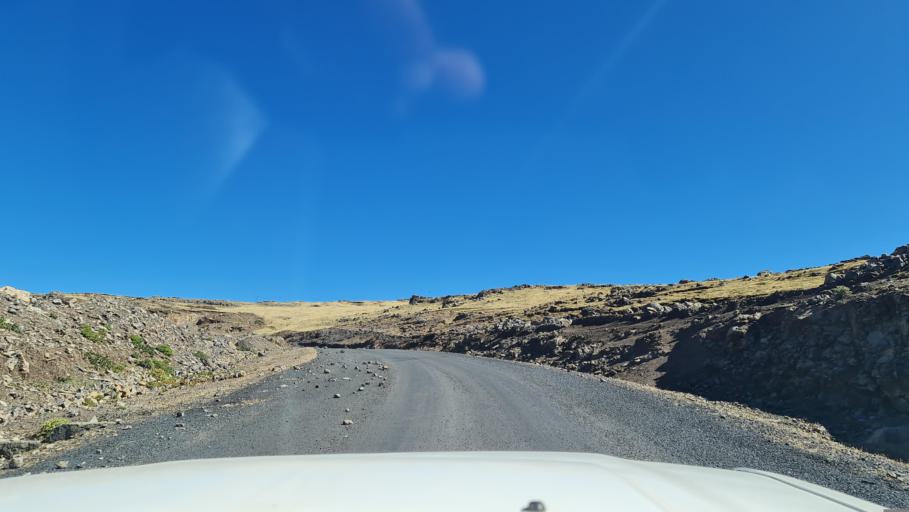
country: ET
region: Amhara
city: Debark'
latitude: 13.1501
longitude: 38.1873
